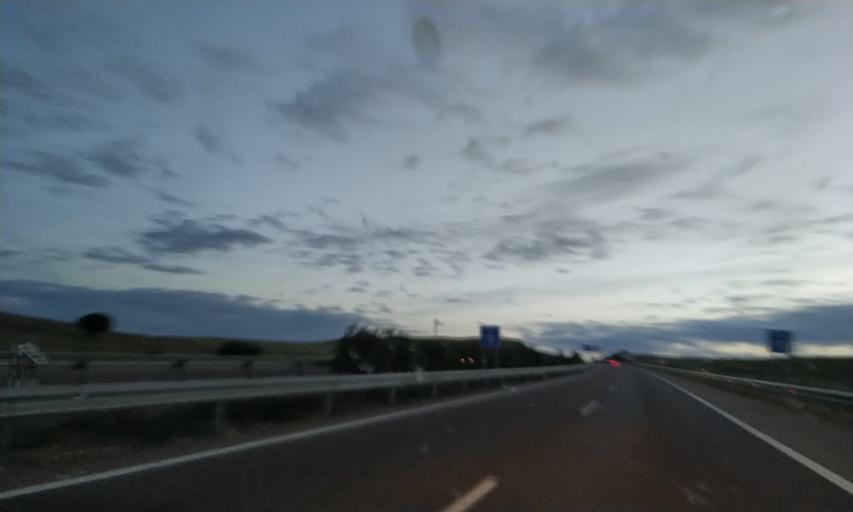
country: ES
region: Extremadura
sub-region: Provincia de Badajoz
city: Badajoz
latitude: 38.9135
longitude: -6.9886
